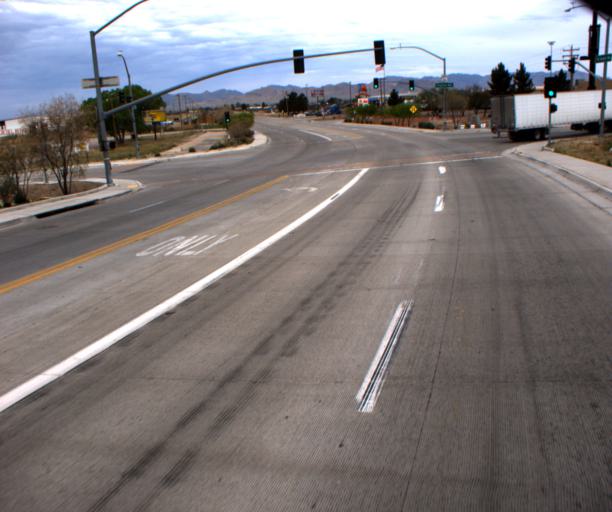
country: US
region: Arizona
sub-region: Cochise County
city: Willcox
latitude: 32.2676
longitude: -109.8460
